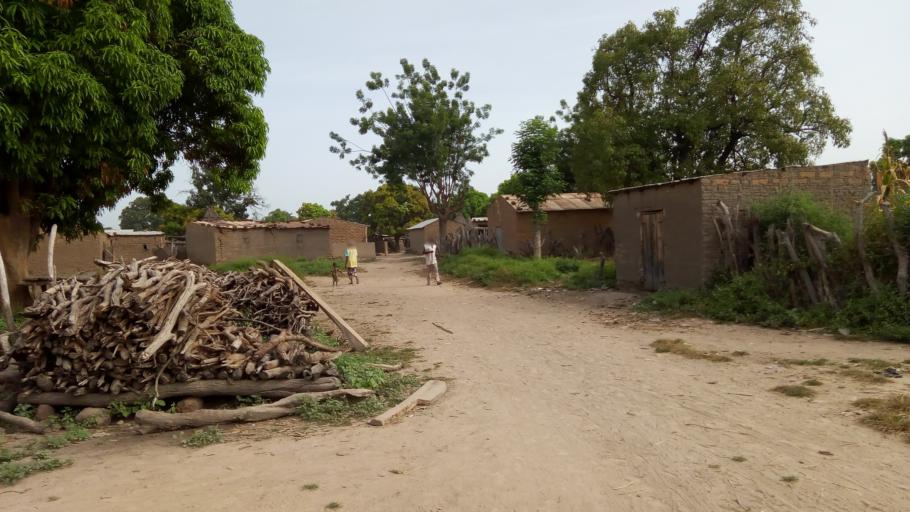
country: ML
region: Kayes
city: Kita
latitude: 13.1979
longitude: -8.7949
